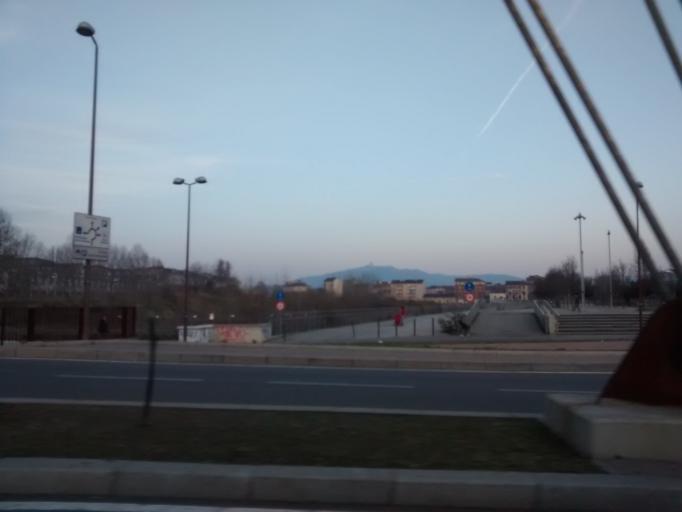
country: IT
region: Piedmont
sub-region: Provincia di Torino
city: Turin
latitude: 45.0898
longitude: 7.6700
